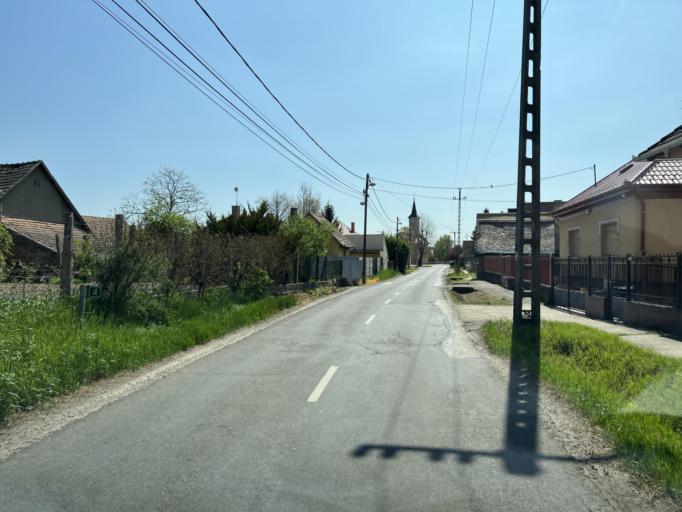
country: HU
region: Pest
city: Ocsa
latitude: 47.2949
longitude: 19.2239
